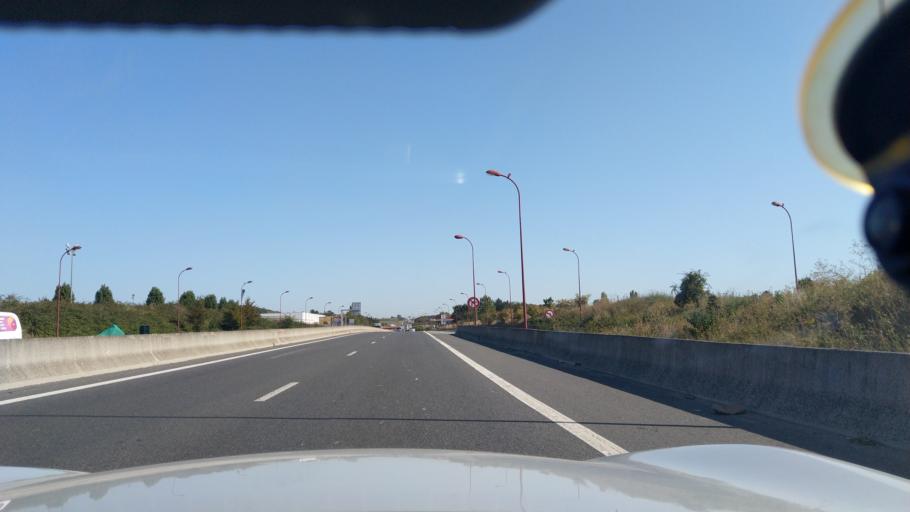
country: FR
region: Ile-de-France
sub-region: Departement du Val-d'Oise
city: Gonesse
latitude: 48.9787
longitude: 2.4652
